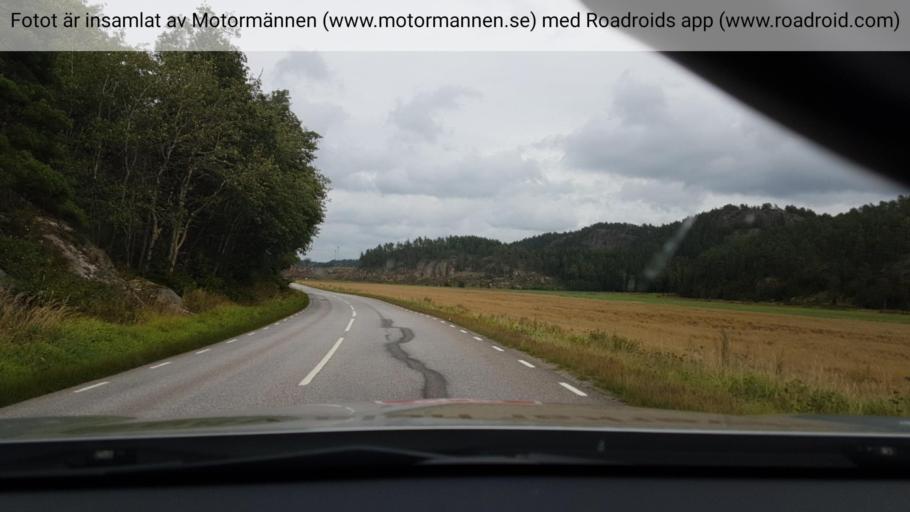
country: SE
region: Vaestra Goetaland
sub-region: Sotenas Kommun
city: Hunnebostrand
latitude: 58.5496
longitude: 11.4333
